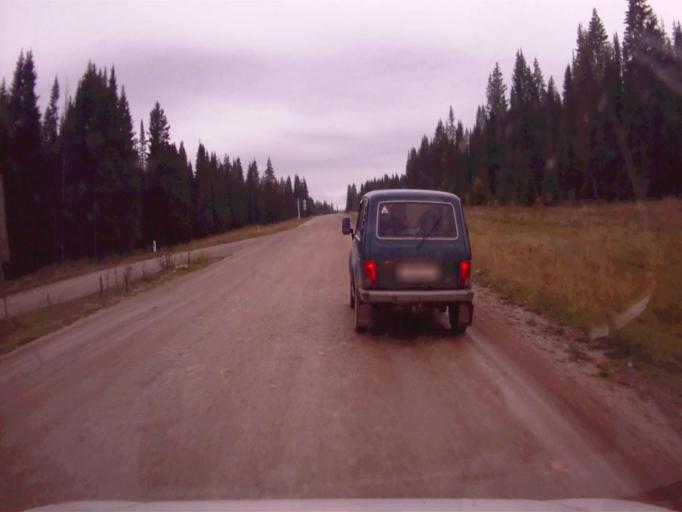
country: RU
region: Chelyabinsk
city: Nyazepetrovsk
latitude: 56.0601
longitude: 59.5619
